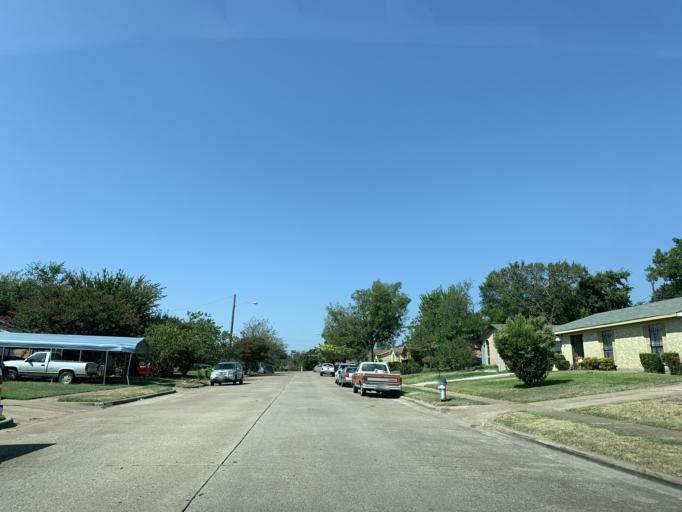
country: US
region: Texas
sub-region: Dallas County
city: Hutchins
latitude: 32.6651
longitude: -96.7557
